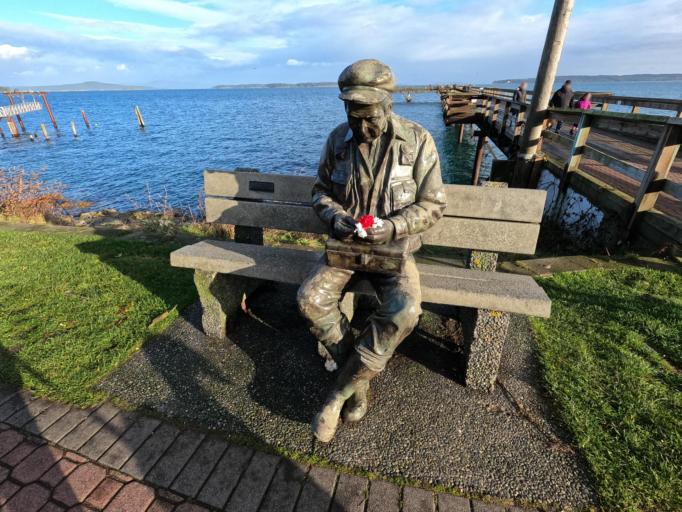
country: CA
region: British Columbia
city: North Saanich
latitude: 48.6477
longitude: -123.3936
